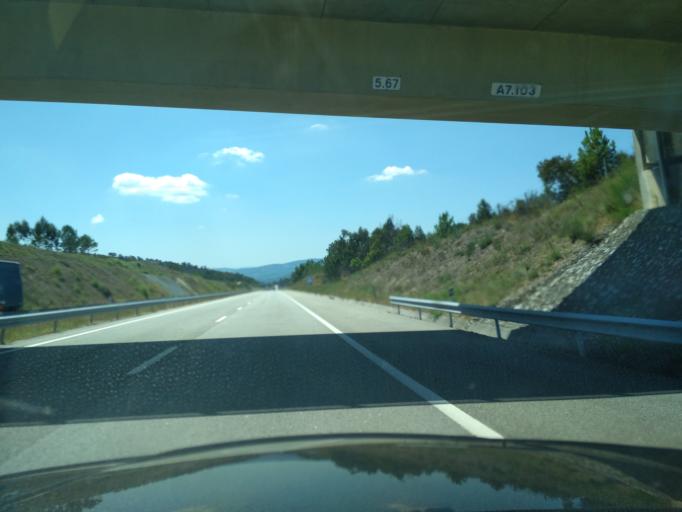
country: PT
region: Braga
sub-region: Fafe
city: Fafe
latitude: 41.4436
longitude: -8.1026
